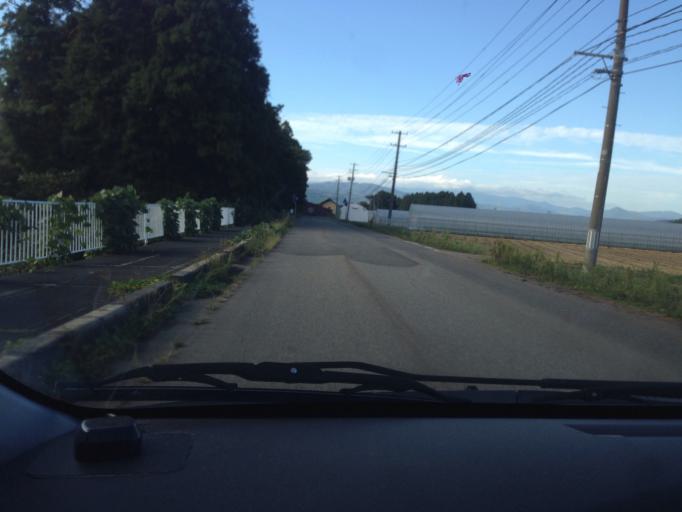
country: JP
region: Fukushima
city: Kitakata
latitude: 37.5871
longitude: 139.7695
